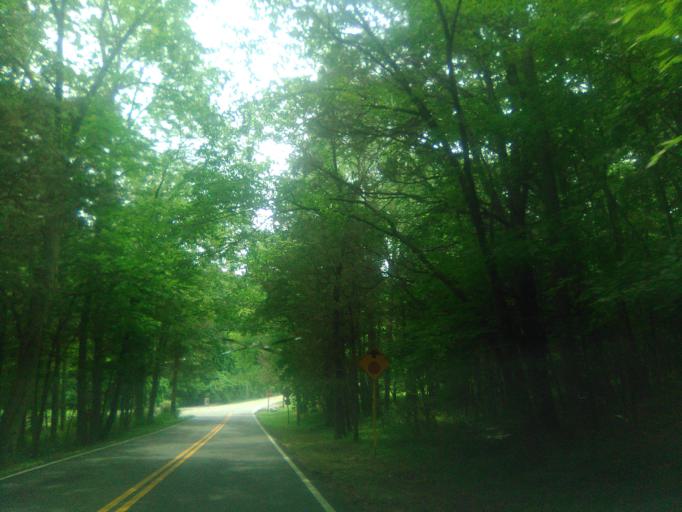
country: US
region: Tennessee
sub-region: Davidson County
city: Forest Hills
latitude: 36.0716
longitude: -86.8715
